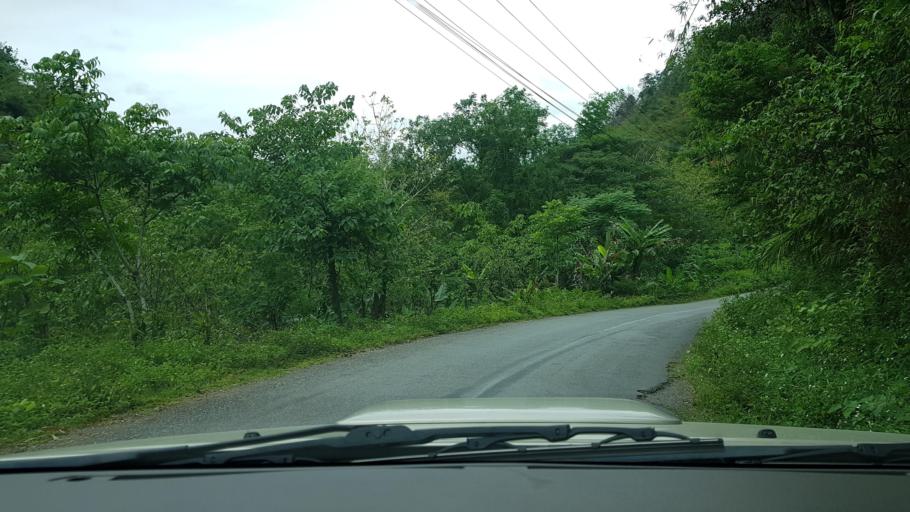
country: LA
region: Phongsali
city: Khoa
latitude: 21.0669
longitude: 102.3801
